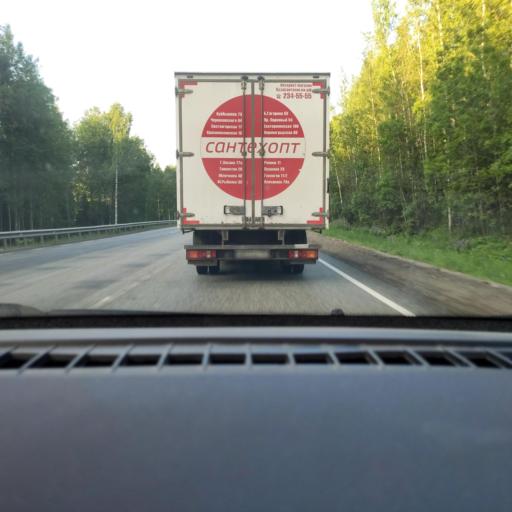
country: RU
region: Perm
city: Pavlovskiy
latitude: 57.9200
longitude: 54.9691
